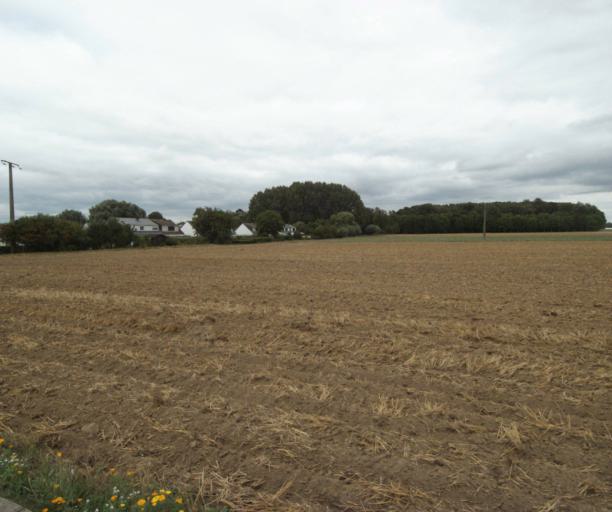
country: FR
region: Nord-Pas-de-Calais
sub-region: Departement du Nord
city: Ennevelin
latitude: 50.5521
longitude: 3.1262
